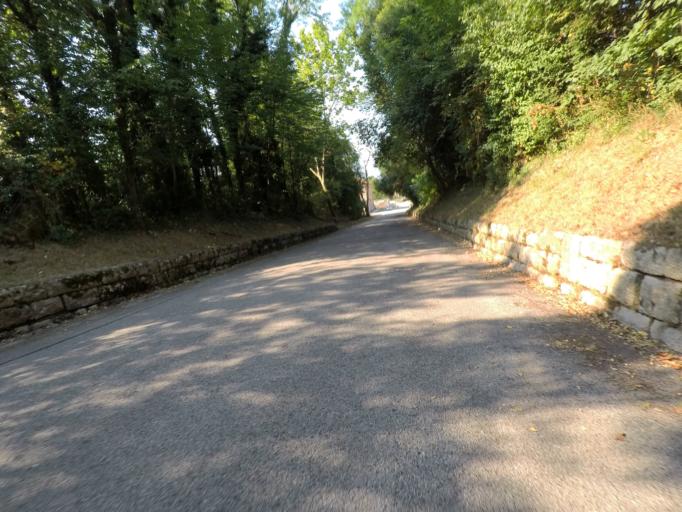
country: IT
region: Friuli Venezia Giulia
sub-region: Provincia di Pordenone
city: Pinzano al Tagliamento
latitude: 46.1803
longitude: 12.9513
